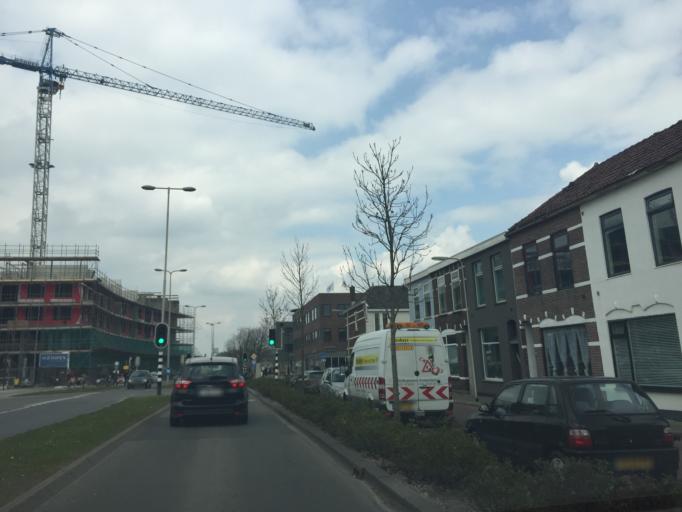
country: NL
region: South Holland
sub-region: Gemeente Alphen aan den Rijn
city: Alphen aan den Rijn
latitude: 52.1246
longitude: 4.6587
